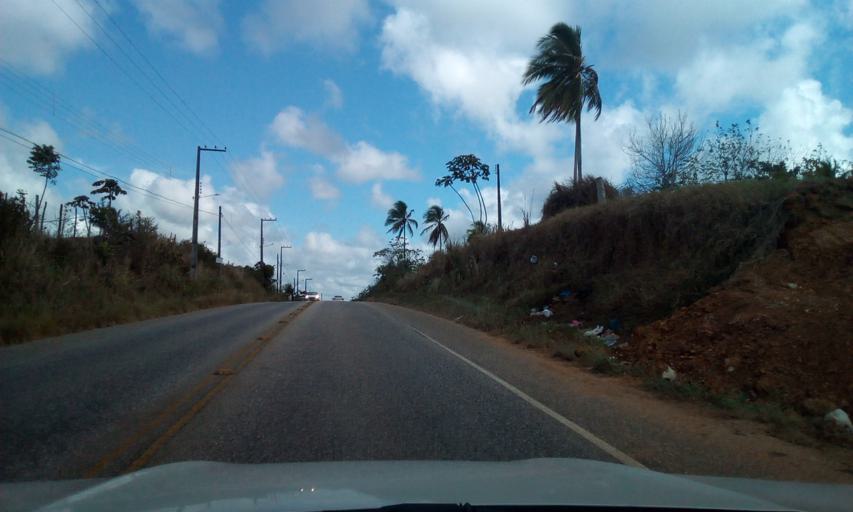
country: BR
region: Sergipe
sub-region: Estancia
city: Estancia
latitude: -11.2931
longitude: -37.4521
